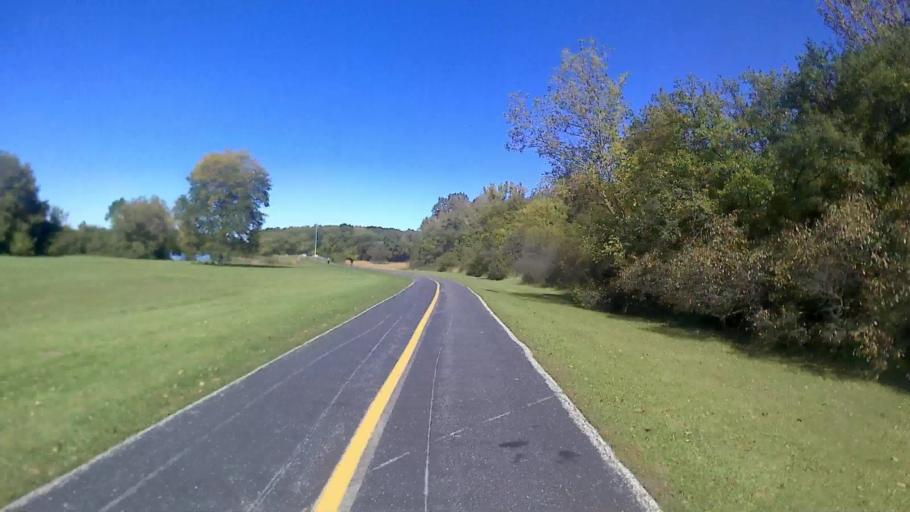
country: US
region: Illinois
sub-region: DuPage County
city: Itasca
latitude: 42.0187
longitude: -88.0150
